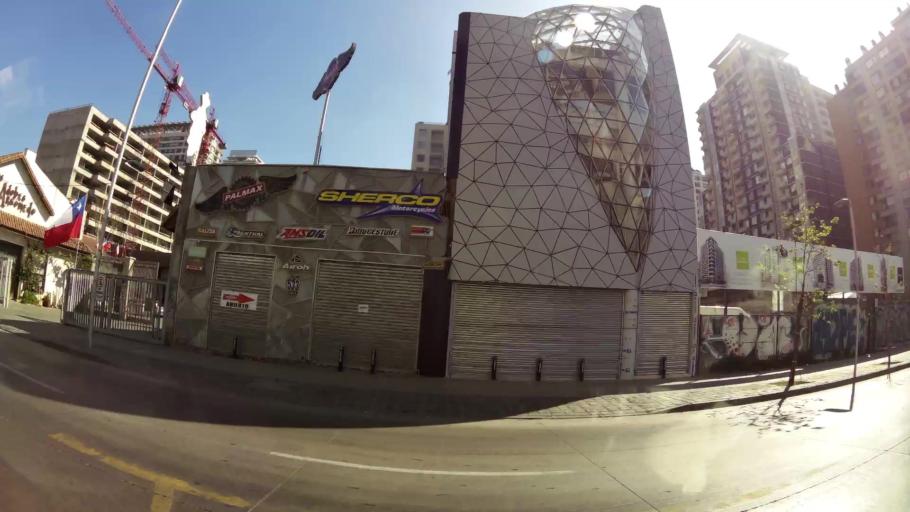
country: CL
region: Santiago Metropolitan
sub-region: Provincia de Santiago
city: Santiago
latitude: -33.4496
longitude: -70.6390
